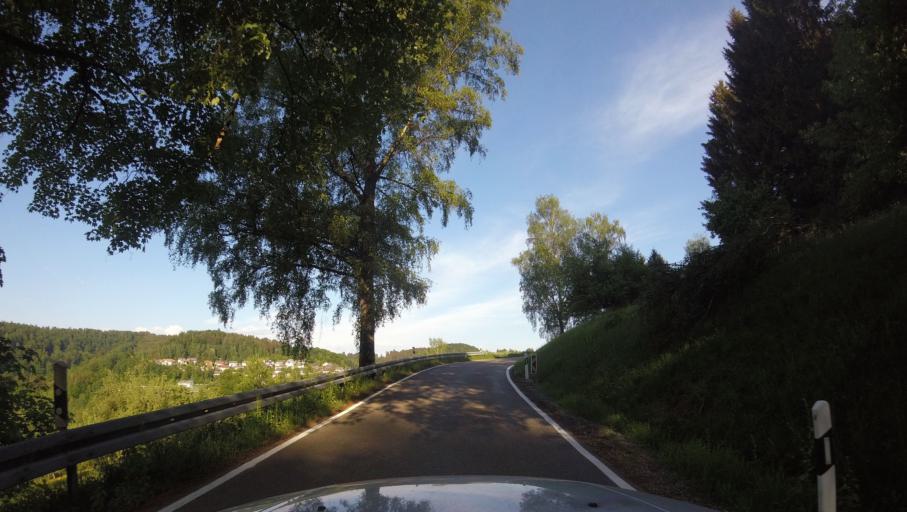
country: DE
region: Baden-Wuerttemberg
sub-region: Regierungsbezirk Stuttgart
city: Spiegelberg
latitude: 49.0358
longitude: 9.4431
